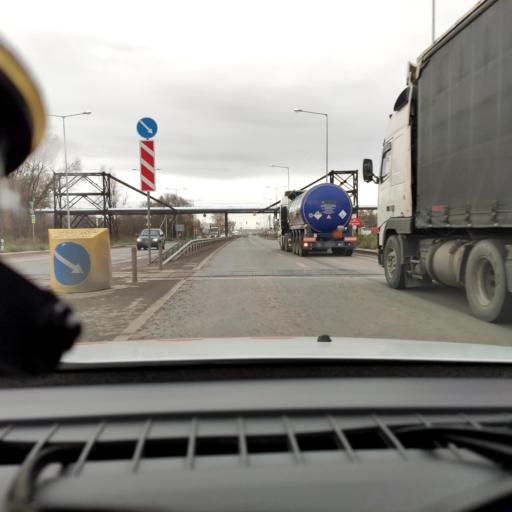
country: RU
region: Samara
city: Smyshlyayevka
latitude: 53.1926
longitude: 50.2940
